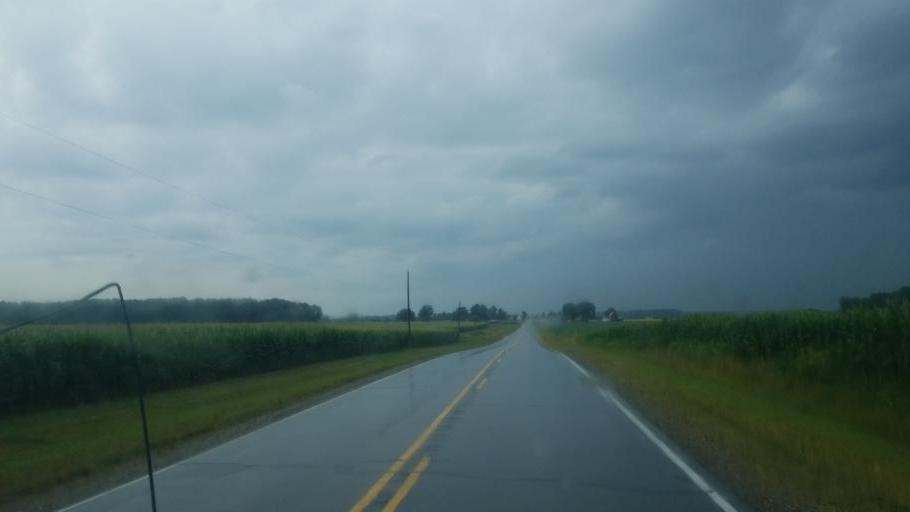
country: US
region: Indiana
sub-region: DeKalb County
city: Butler
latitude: 41.4735
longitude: -84.8720
